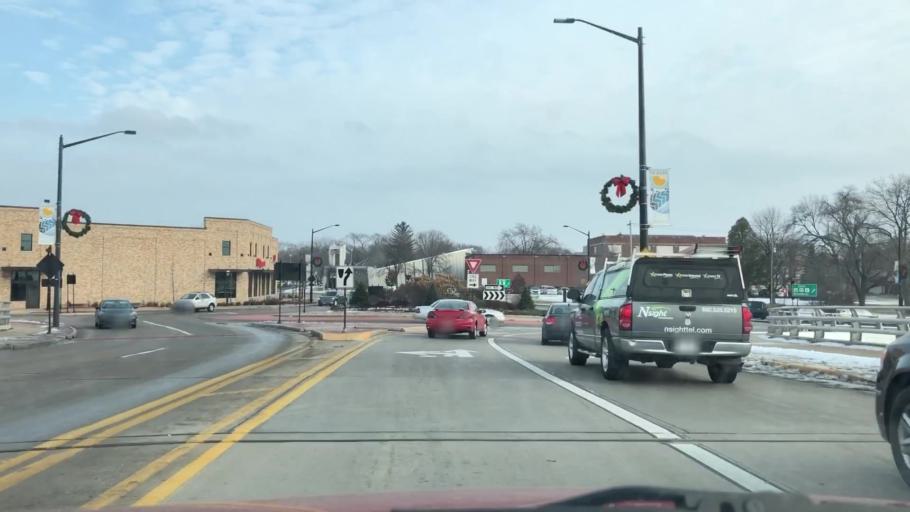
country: US
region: Wisconsin
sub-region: Brown County
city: De Pere
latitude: 44.4475
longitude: -88.0613
